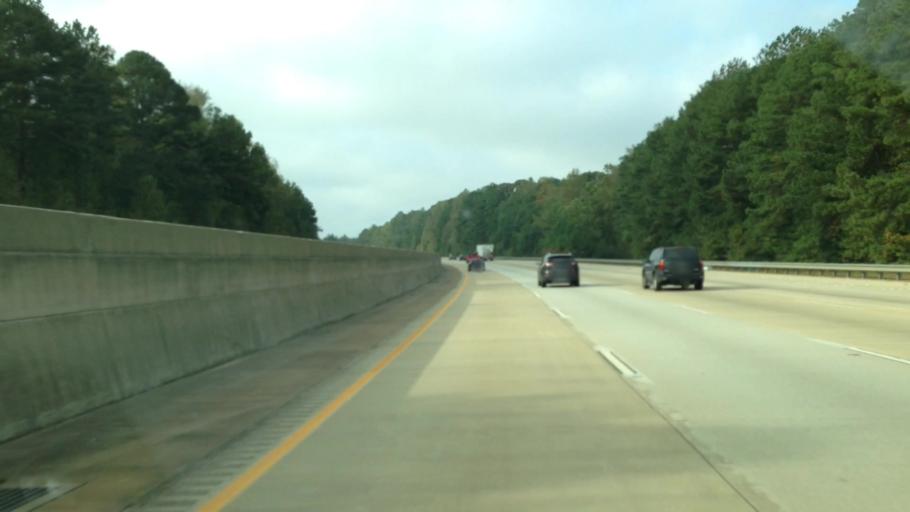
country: US
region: Georgia
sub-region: Coweta County
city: Newnan
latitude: 33.4282
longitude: -84.7219
